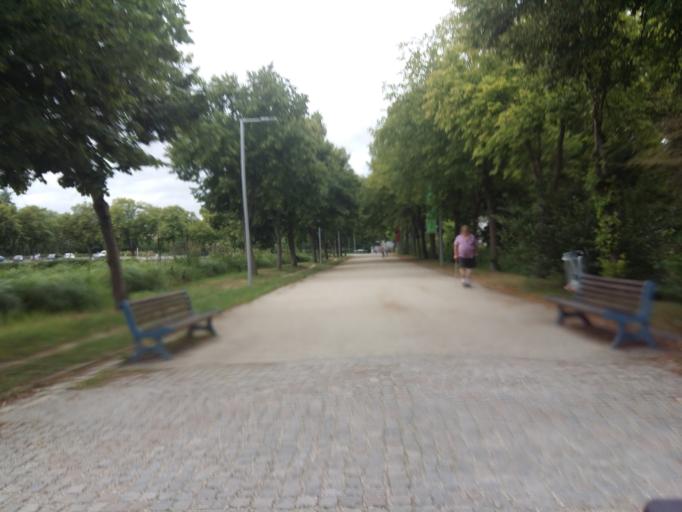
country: FR
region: Picardie
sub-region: Departement de la Somme
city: Amiens
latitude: 49.8997
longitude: 2.2762
